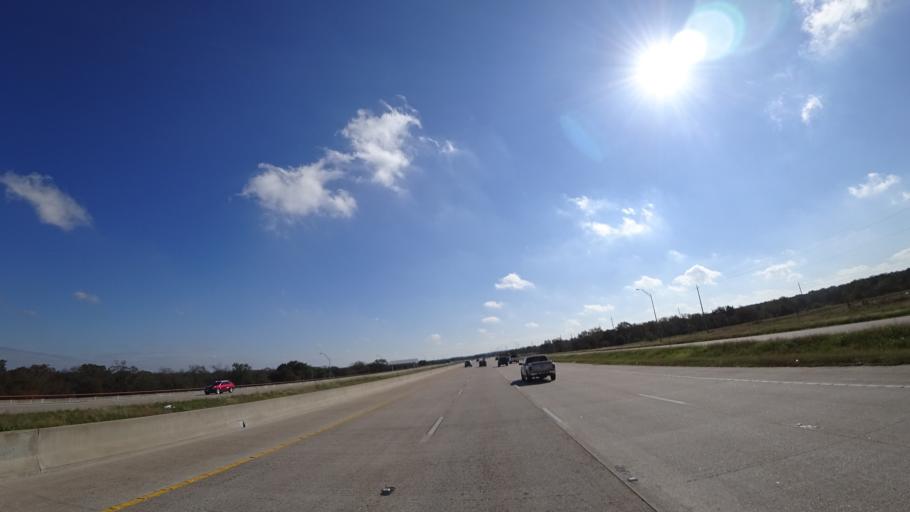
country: US
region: Texas
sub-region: Williamson County
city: Brushy Creek
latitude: 30.4802
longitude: -97.7378
